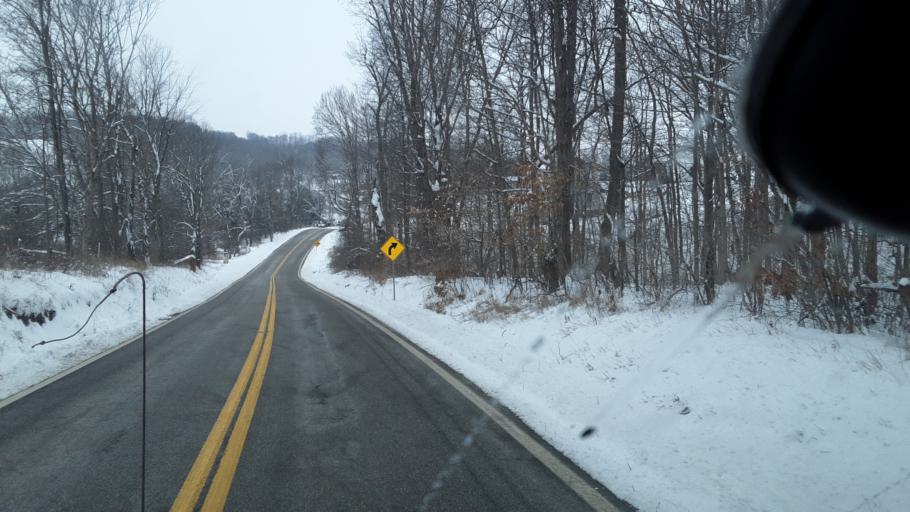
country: US
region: Ohio
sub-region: Perry County
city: Somerset
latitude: 39.8538
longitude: -82.2570
